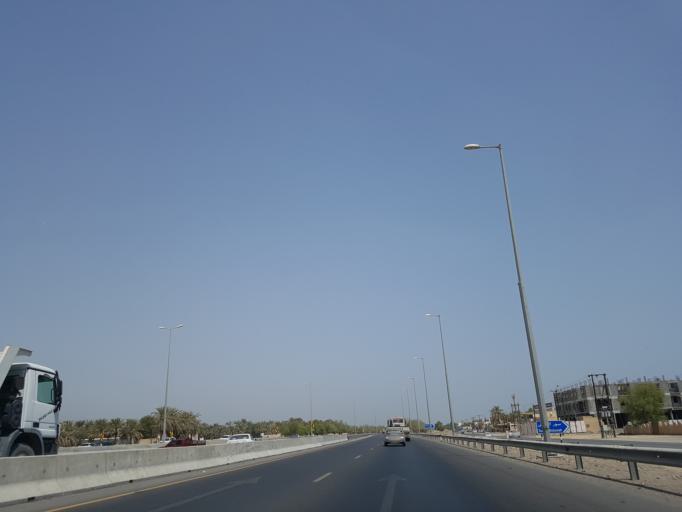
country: OM
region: Al Batinah
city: Saham
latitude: 24.1549
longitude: 56.8673
